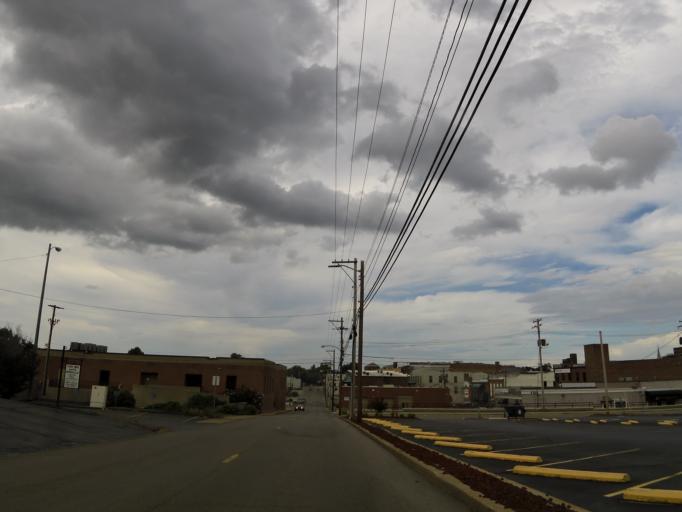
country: US
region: Kentucky
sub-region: Christian County
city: Hopkinsville
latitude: 36.8645
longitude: -87.4908
